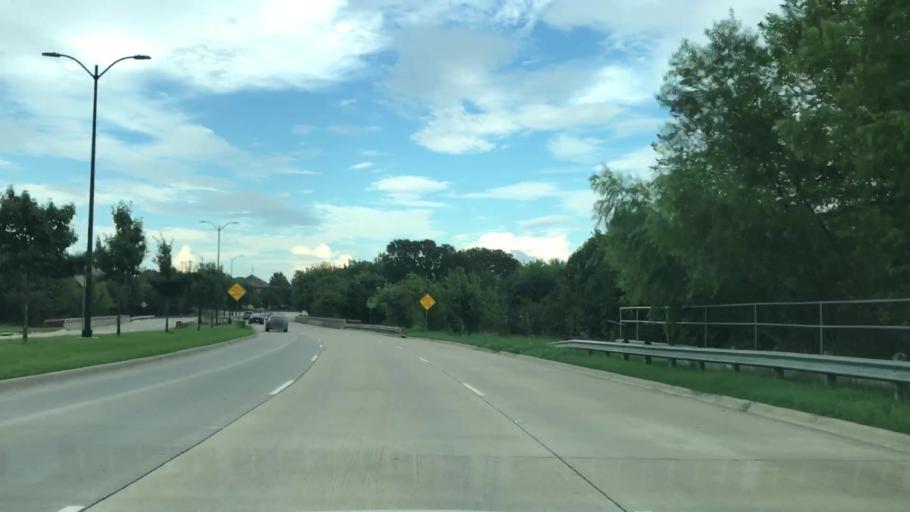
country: US
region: Texas
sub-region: Collin County
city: Frisco
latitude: 33.1746
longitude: -96.8013
